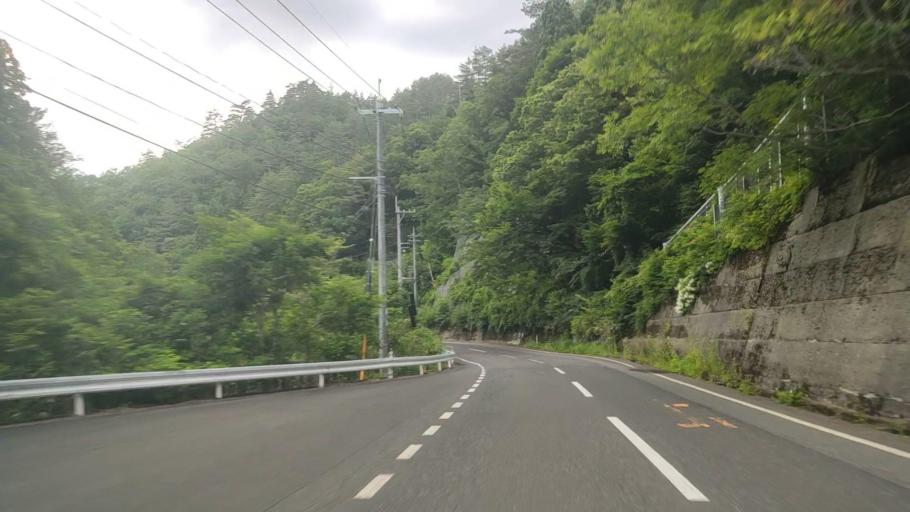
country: JP
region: Tottori
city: Kurayoshi
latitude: 35.2912
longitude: 133.9648
